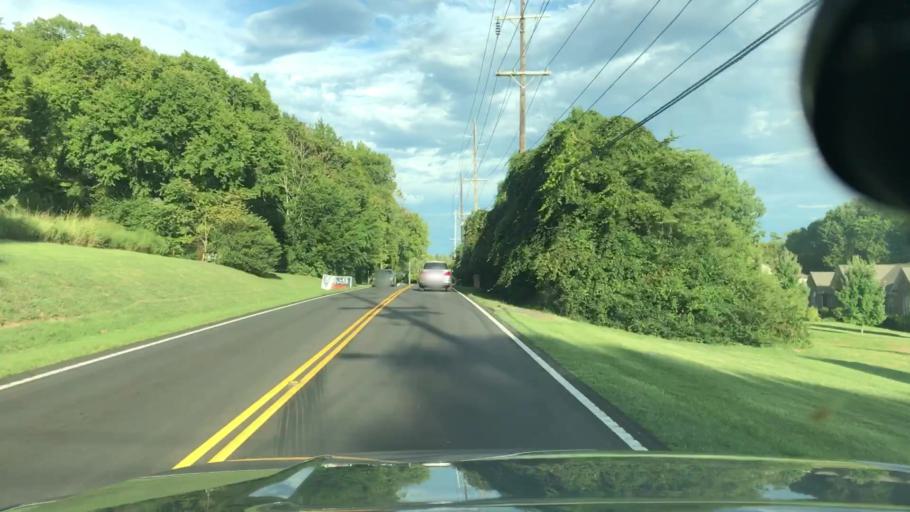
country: US
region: Tennessee
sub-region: Davidson County
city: Forest Hills
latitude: 36.0423
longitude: -86.8369
